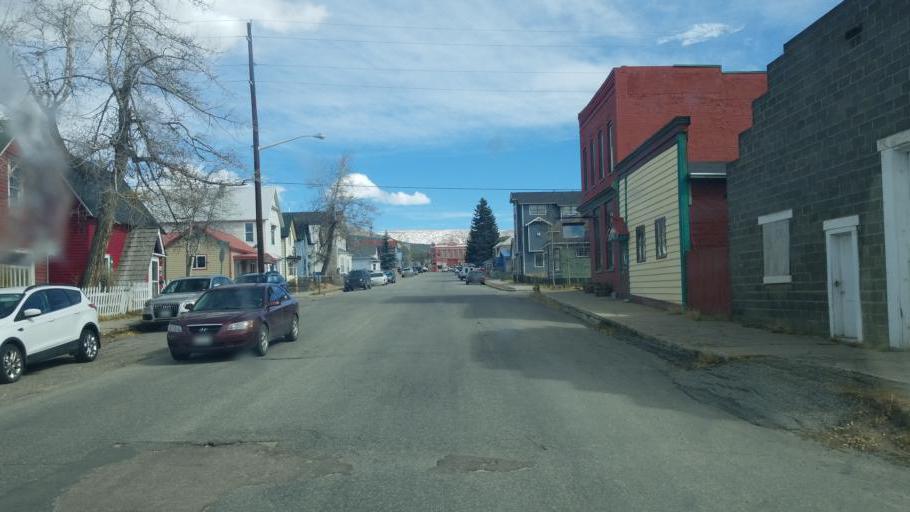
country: US
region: Colorado
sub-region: Lake County
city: Leadville
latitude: 39.2481
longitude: -106.2945
